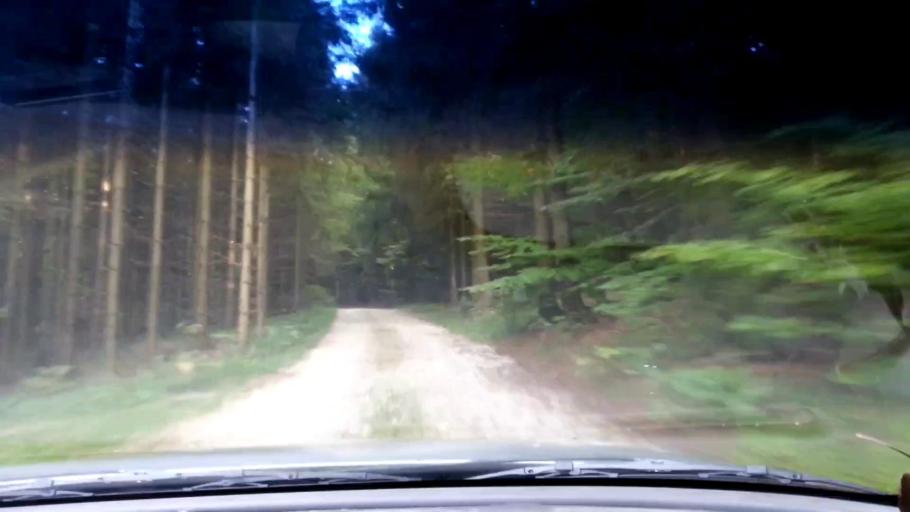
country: DE
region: Bavaria
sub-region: Upper Franconia
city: Wattendorf
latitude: 49.9964
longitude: 11.1070
